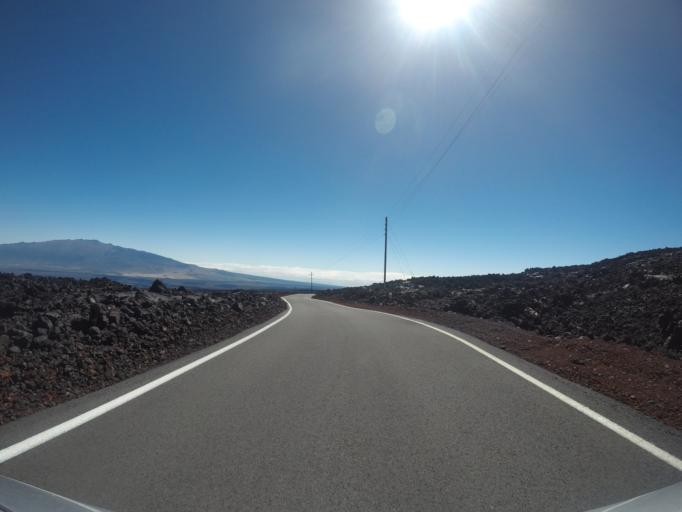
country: US
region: Hawaii
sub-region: Hawaii County
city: Volcano
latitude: 19.5541
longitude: -155.5374
